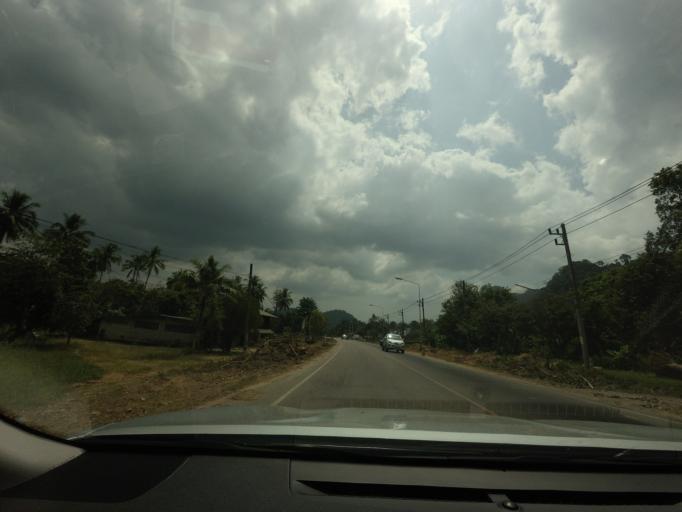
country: TH
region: Phangnga
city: Ban Ao Nang
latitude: 8.1004
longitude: 98.8019
